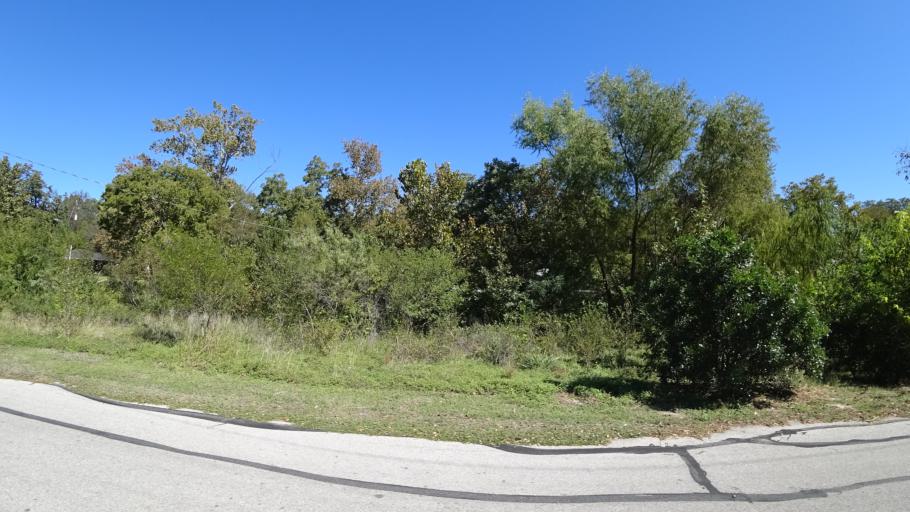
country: US
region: Texas
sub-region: Travis County
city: Austin
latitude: 30.2931
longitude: -97.7120
